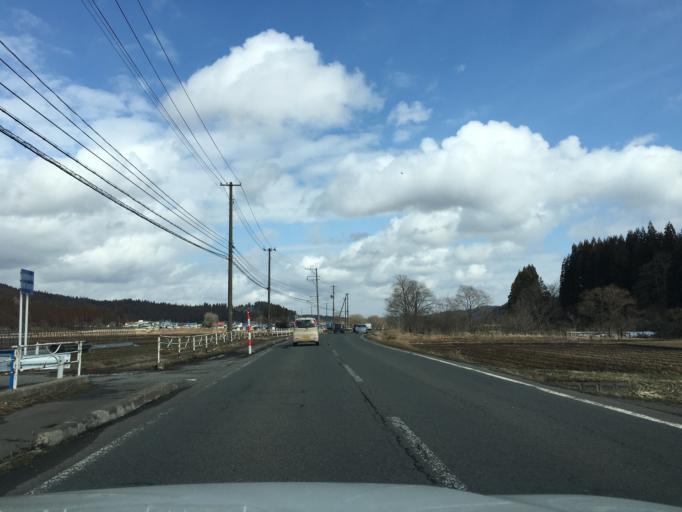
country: JP
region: Akita
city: Takanosu
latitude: 40.0375
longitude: 140.2776
